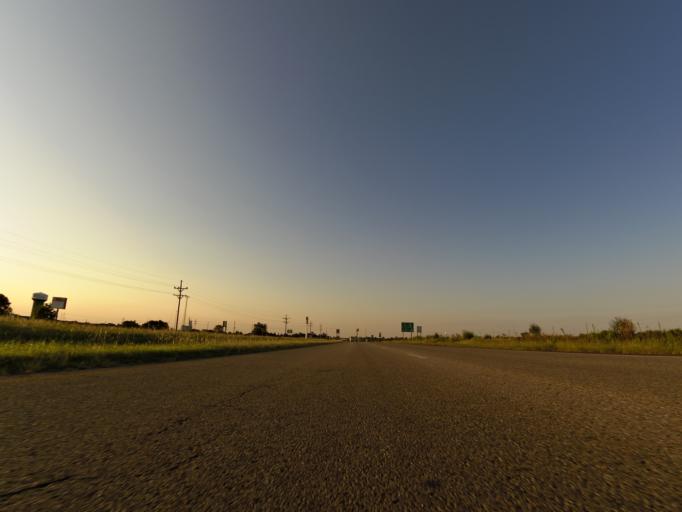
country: US
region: Kansas
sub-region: Reno County
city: South Hutchinson
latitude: 38.0084
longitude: -97.9402
